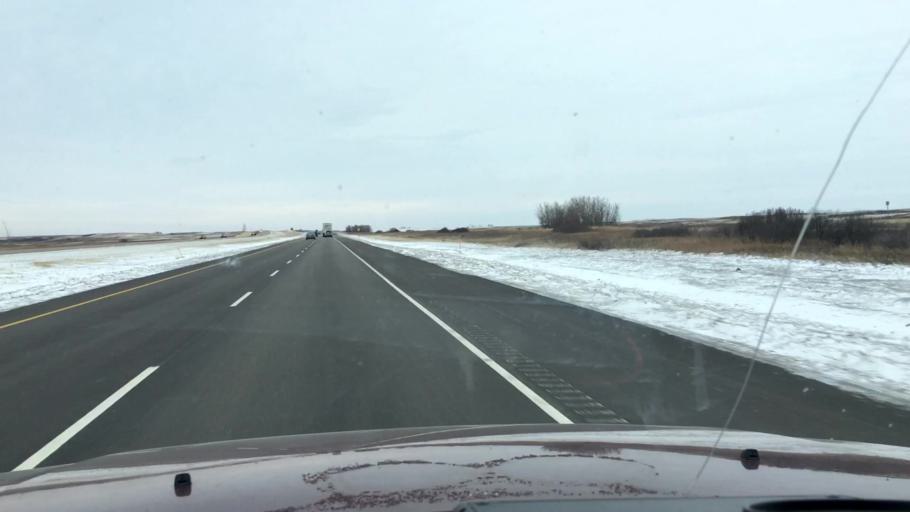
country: CA
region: Saskatchewan
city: Moose Jaw
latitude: 50.8895
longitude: -105.6250
